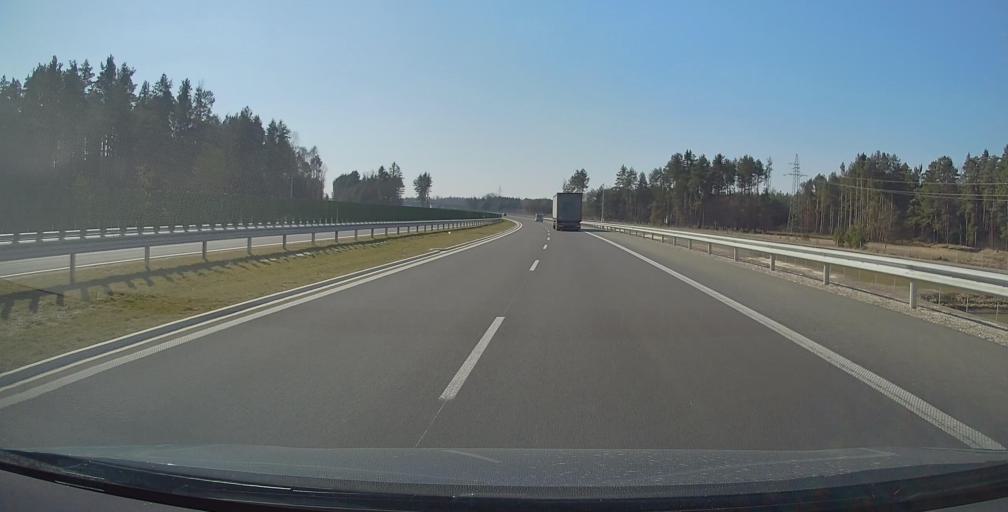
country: PL
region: Subcarpathian Voivodeship
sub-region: Powiat nizanski
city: Konczyce
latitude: 50.4301
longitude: 22.1321
